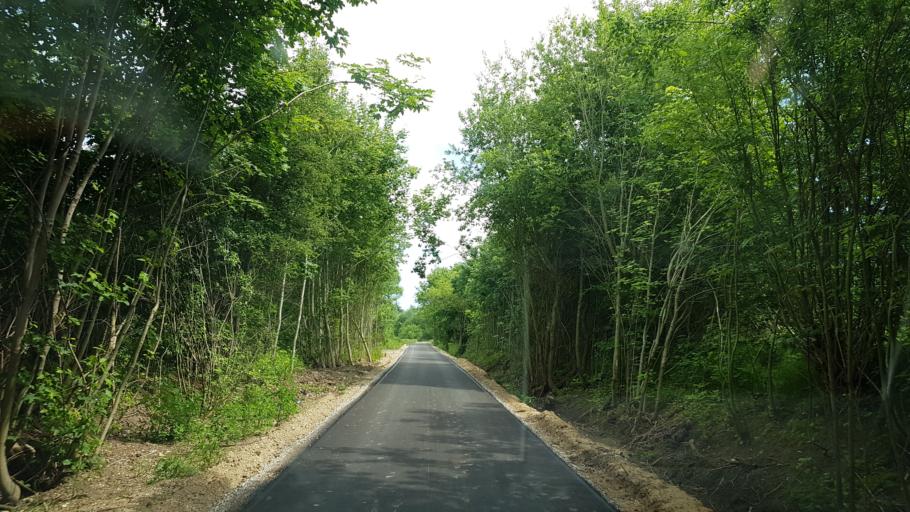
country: PL
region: Pomeranian Voivodeship
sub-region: Powiat slupski
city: Ustka
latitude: 54.5148
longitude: 16.7376
